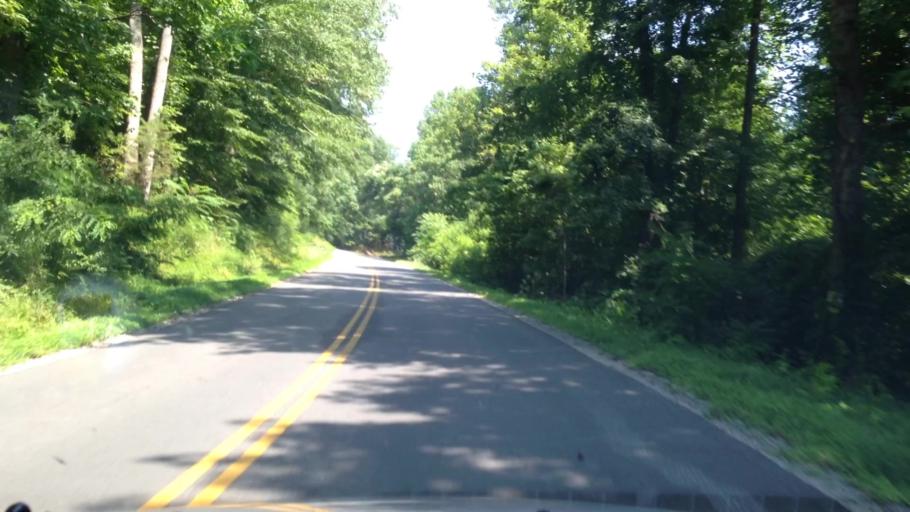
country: US
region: Virginia
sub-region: Patrick County
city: Patrick Springs
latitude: 36.6005
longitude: -80.1694
